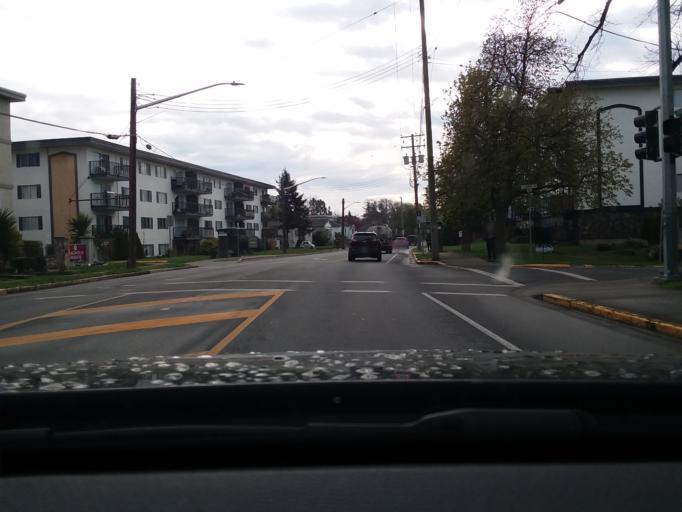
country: CA
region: British Columbia
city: Victoria
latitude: 48.4402
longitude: -123.3961
